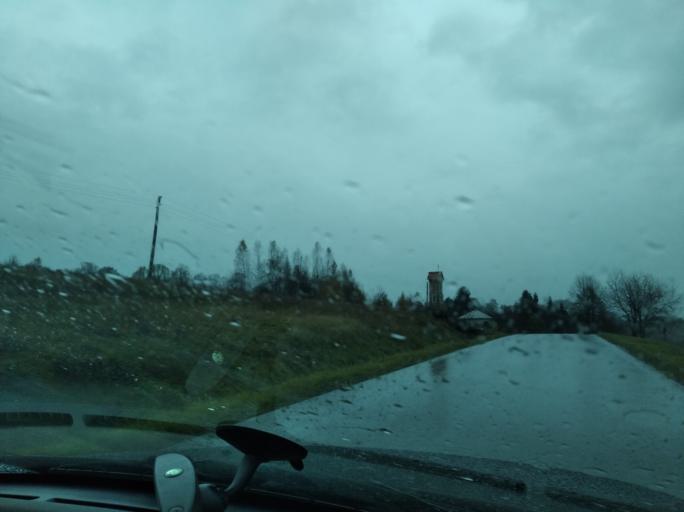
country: PL
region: Subcarpathian Voivodeship
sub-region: Powiat rzeszowski
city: Chmielnik
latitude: 49.9771
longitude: 22.1719
